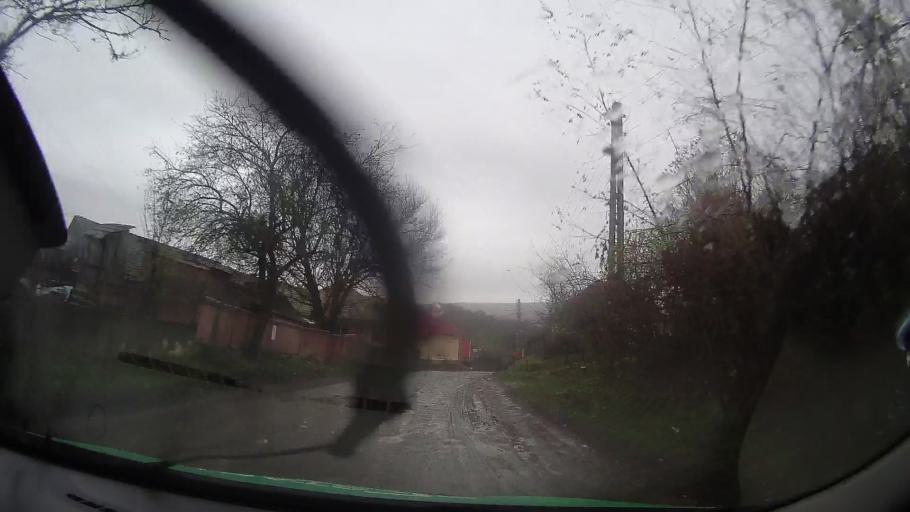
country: RO
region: Bistrita-Nasaud
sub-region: Comuna Monor
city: Monor
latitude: 46.9502
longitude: 24.7048
